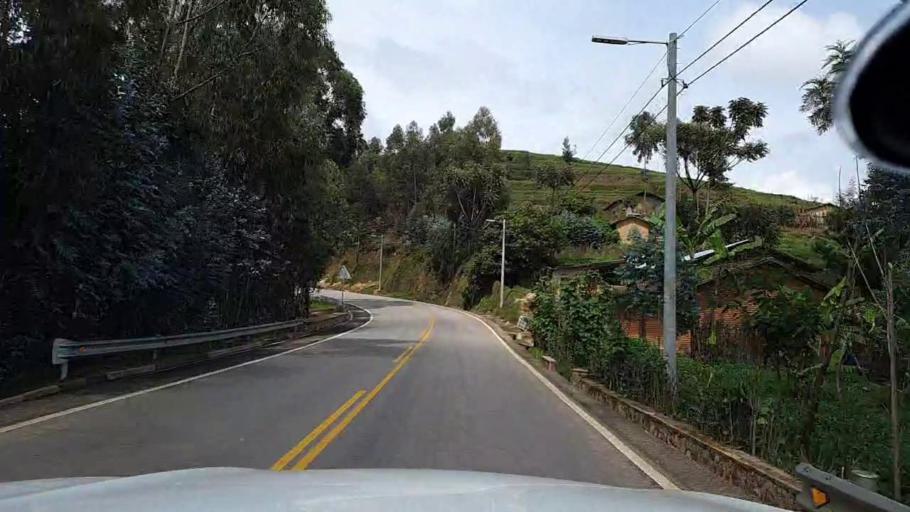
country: RW
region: Southern Province
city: Nzega
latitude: -2.5200
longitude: 29.4562
